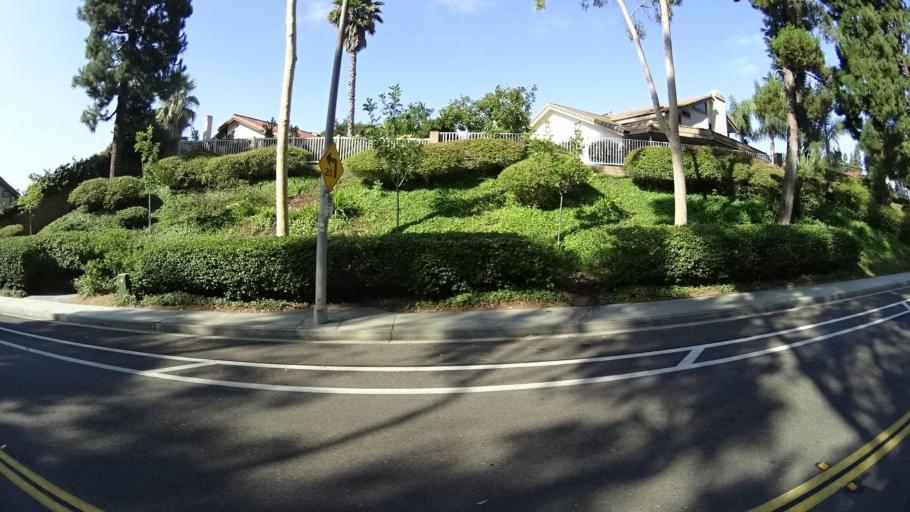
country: US
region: California
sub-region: San Diego County
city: Vista
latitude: 33.1708
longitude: -117.2296
